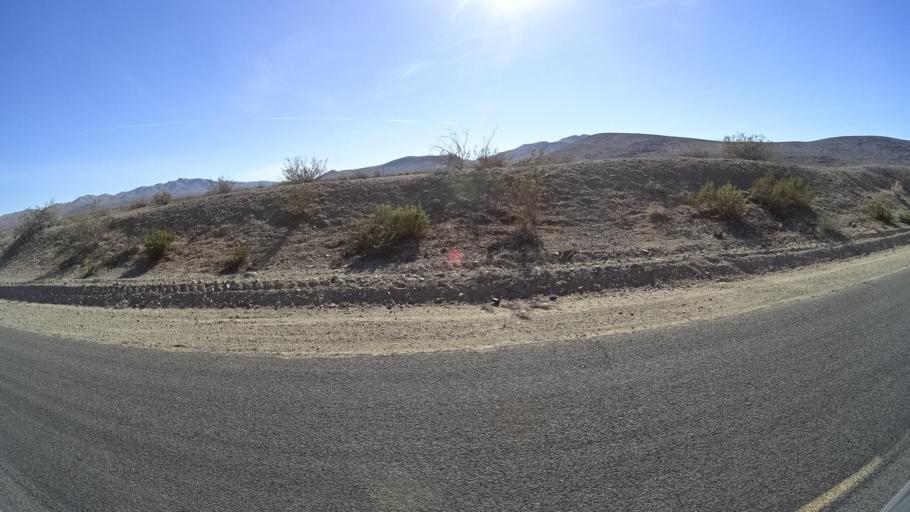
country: US
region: California
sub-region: Kern County
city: China Lake Acres
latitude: 35.5572
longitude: -117.7506
